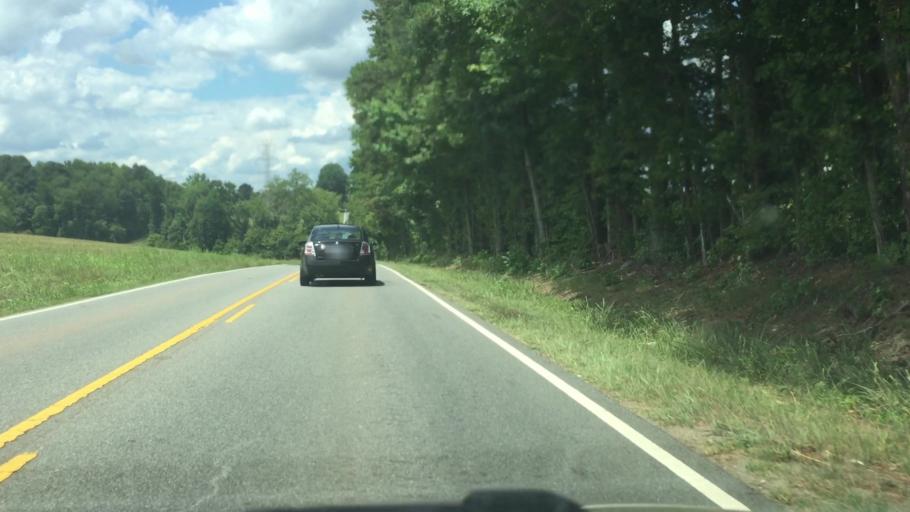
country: US
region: North Carolina
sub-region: Rowan County
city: Enochville
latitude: 35.4854
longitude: -80.6986
